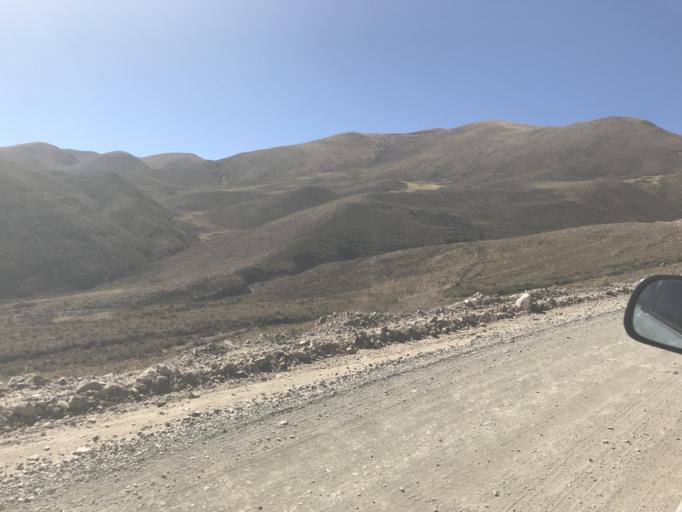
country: AR
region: Jujuy
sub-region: Departamento de Humahuaca
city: Humahuaca
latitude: -23.1953
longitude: -65.2217
